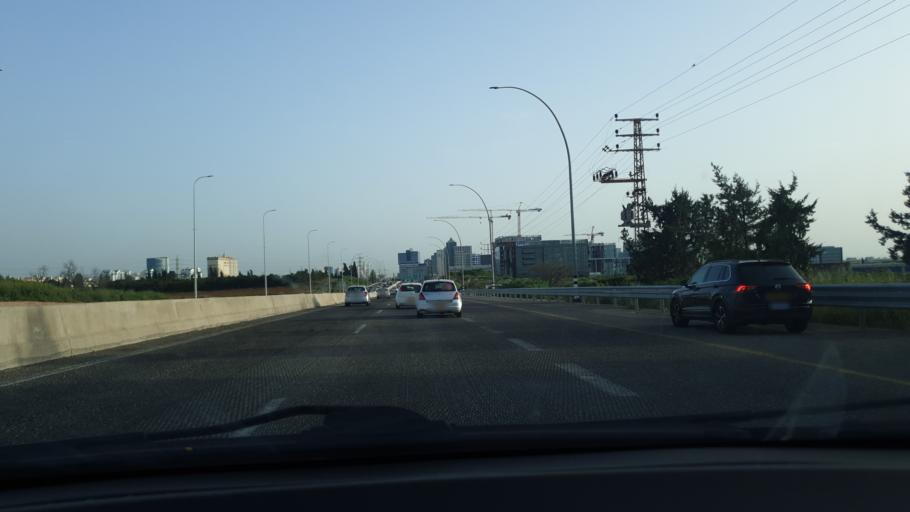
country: IL
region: Central District
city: Ra'anana
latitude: 32.2067
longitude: 34.8840
